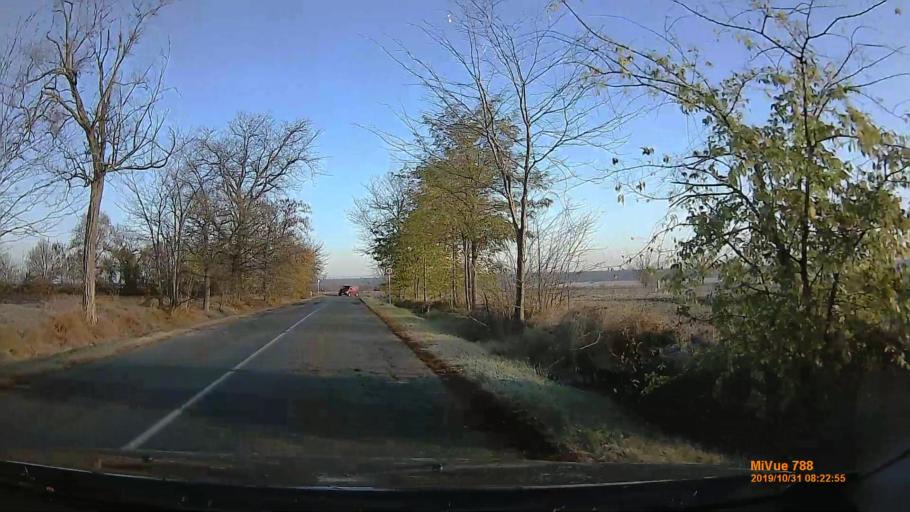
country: HU
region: Pest
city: Pand
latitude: 47.3681
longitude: 19.6398
